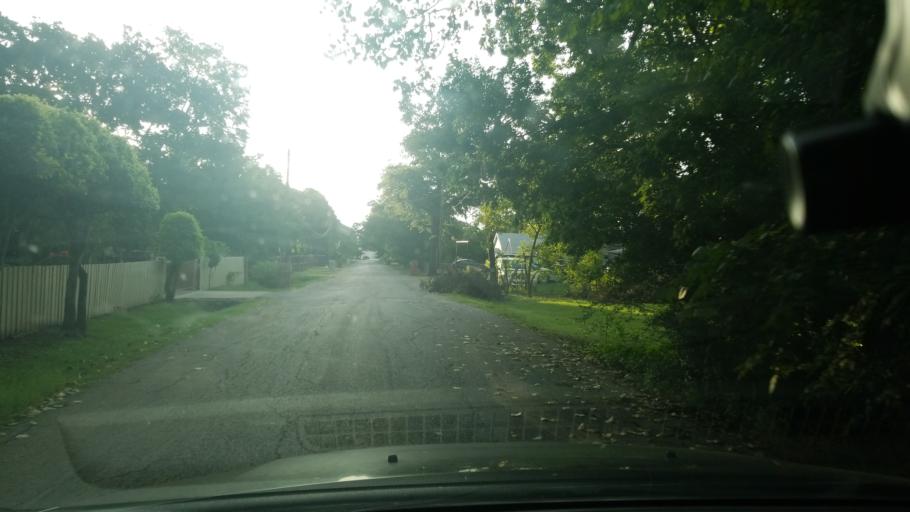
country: US
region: Texas
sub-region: Dallas County
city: Balch Springs
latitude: 32.7459
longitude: -96.6372
